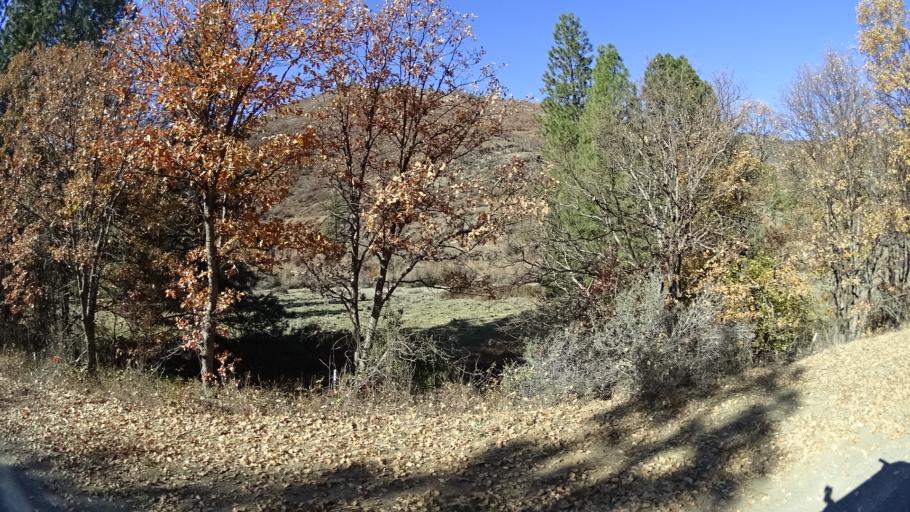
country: US
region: California
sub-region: Siskiyou County
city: Yreka
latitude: 41.8467
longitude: -122.8363
